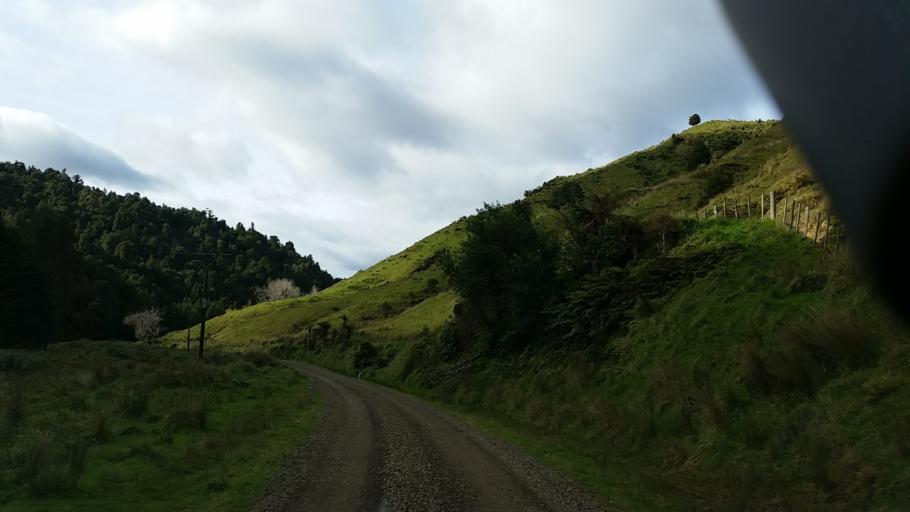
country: NZ
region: Taranaki
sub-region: New Plymouth District
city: Waitara
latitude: -39.0393
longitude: 174.5918
